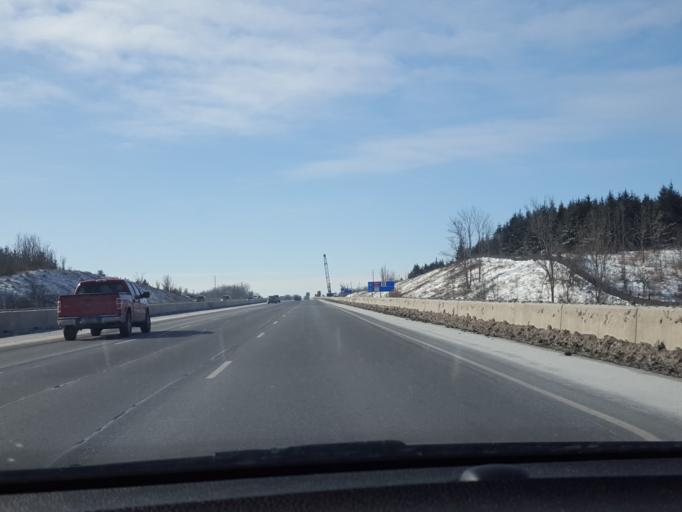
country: CA
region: Ontario
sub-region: Halton
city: Milton
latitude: 43.5081
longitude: -79.9536
